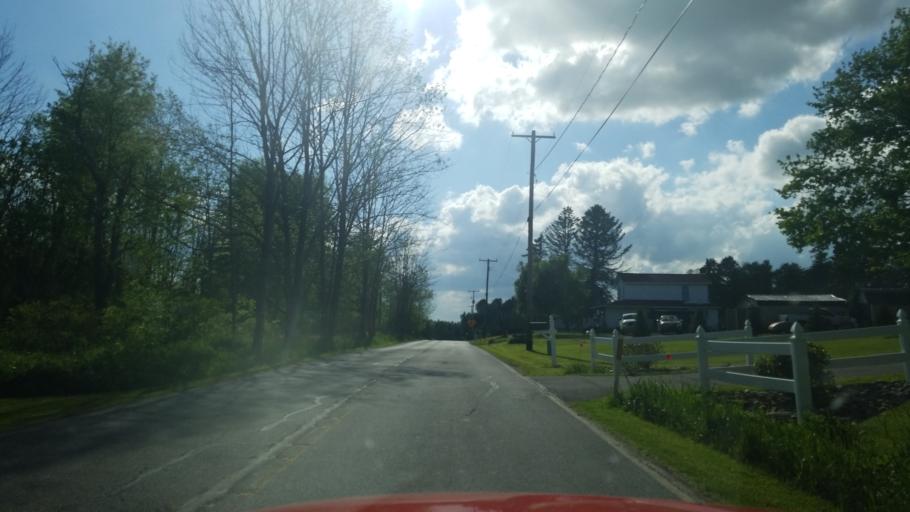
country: US
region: Pennsylvania
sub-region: Clearfield County
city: Hyde
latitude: 40.9754
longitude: -78.4542
